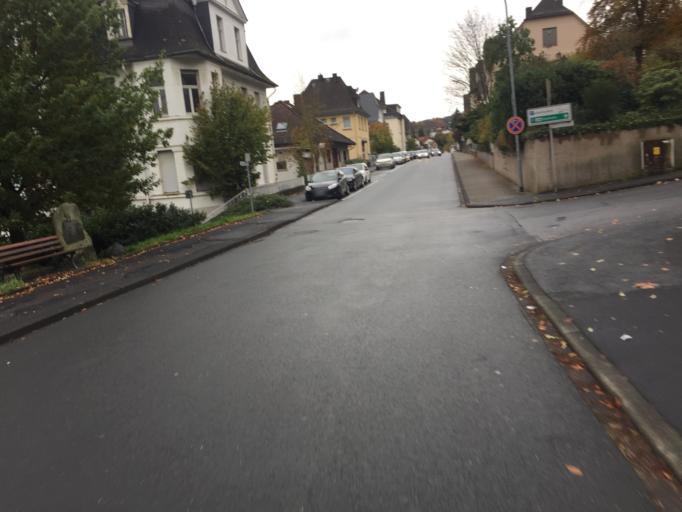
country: DE
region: Hesse
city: Dillenburg
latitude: 50.7431
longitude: 8.2868
